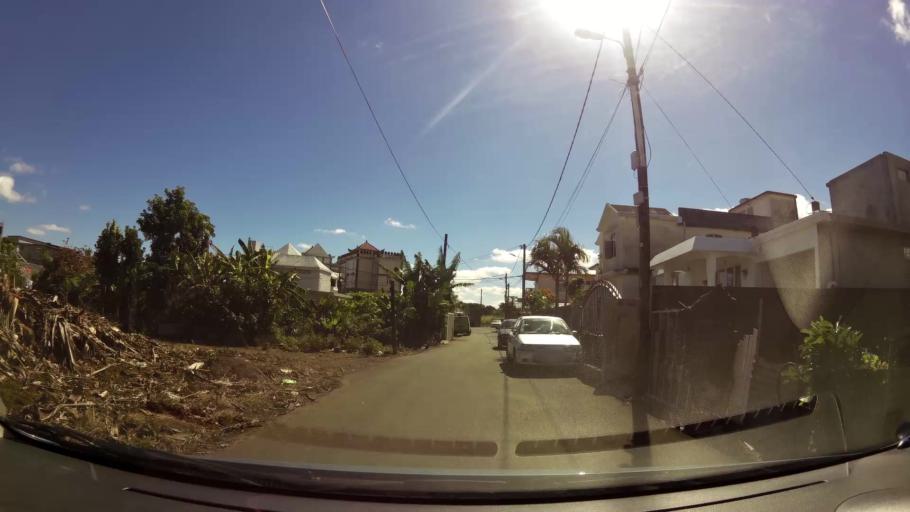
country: MU
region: Plaines Wilhems
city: Vacoas
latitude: -20.3337
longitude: 57.4781
